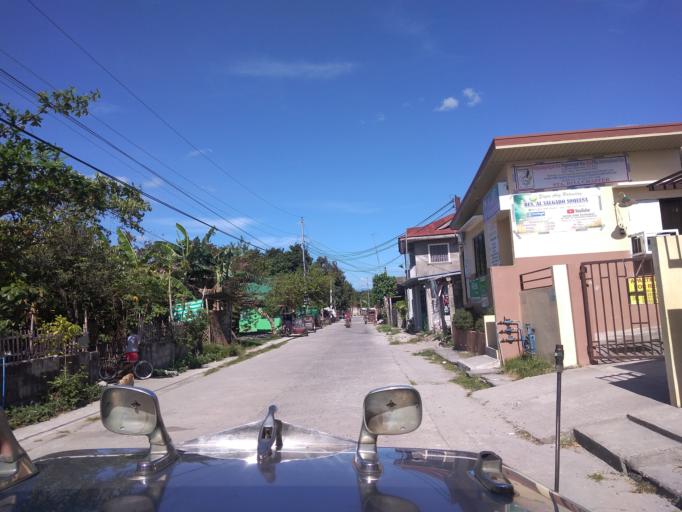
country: PH
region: Central Luzon
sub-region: Province of Pampanga
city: San Agustin
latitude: 14.9909
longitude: 120.6025
